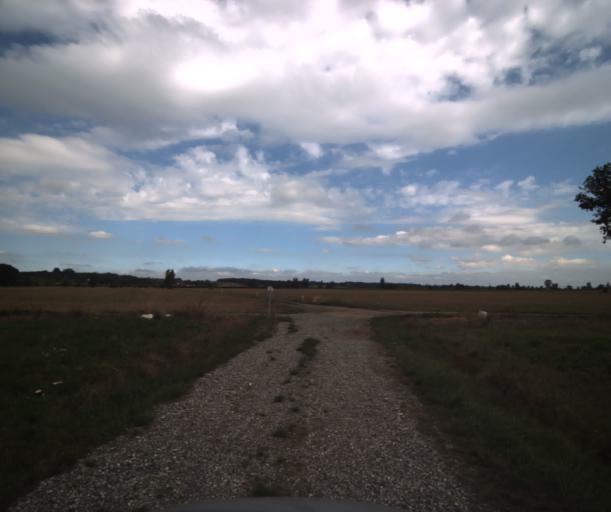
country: FR
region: Midi-Pyrenees
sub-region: Departement de la Haute-Garonne
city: Lherm
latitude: 43.3948
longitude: 1.2298
